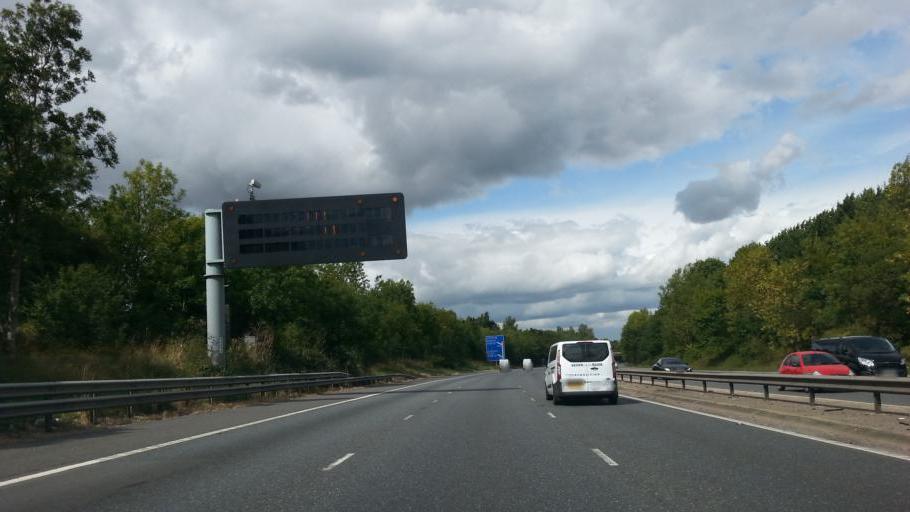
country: GB
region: England
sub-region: Essex
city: Little Hallingbury
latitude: 51.8454
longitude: 0.1871
